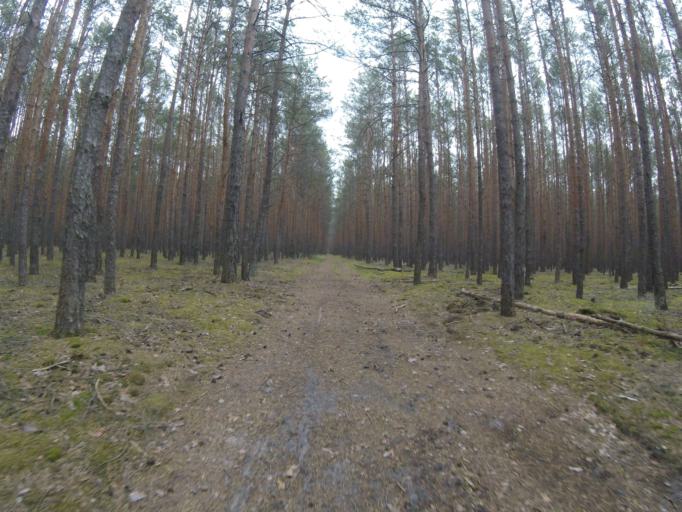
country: DE
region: Brandenburg
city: Halbe
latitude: 52.1087
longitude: 13.7111
